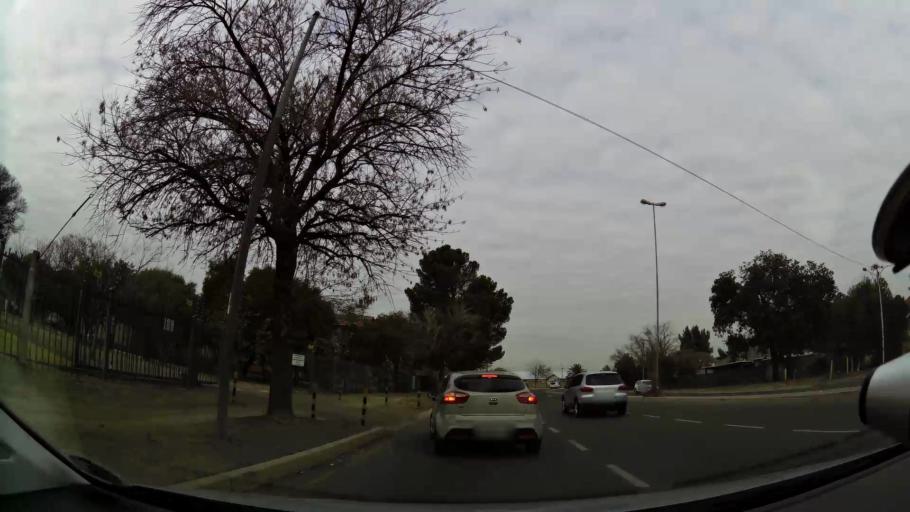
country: ZA
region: Orange Free State
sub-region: Mangaung Metropolitan Municipality
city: Bloemfontein
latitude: -29.1226
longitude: 26.1984
